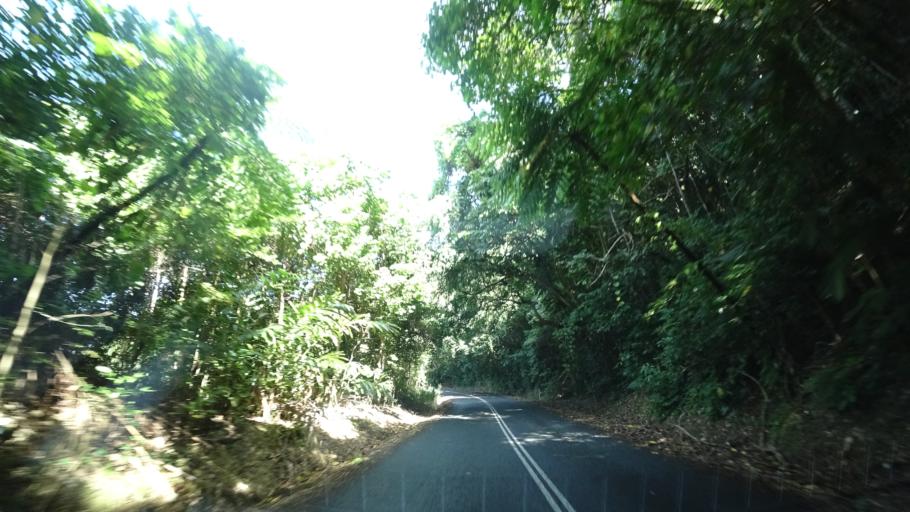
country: AU
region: Queensland
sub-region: Cairns
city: Port Douglas
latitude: -16.1228
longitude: 145.4575
